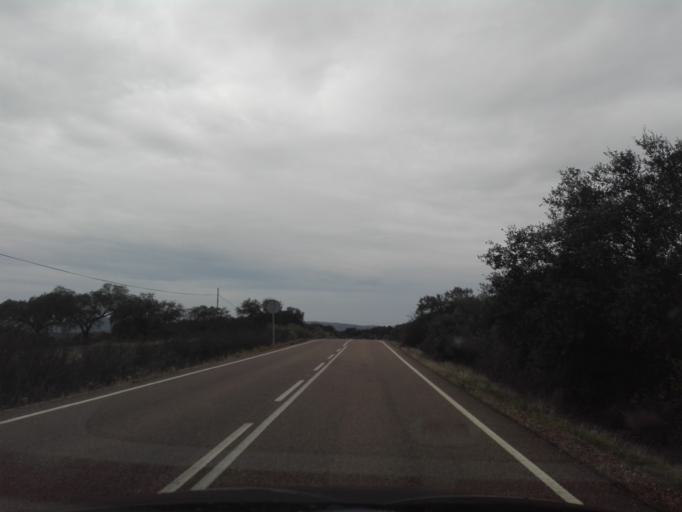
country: ES
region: Extremadura
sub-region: Provincia de Badajoz
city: Alburquerque
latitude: 39.1994
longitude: -7.0019
